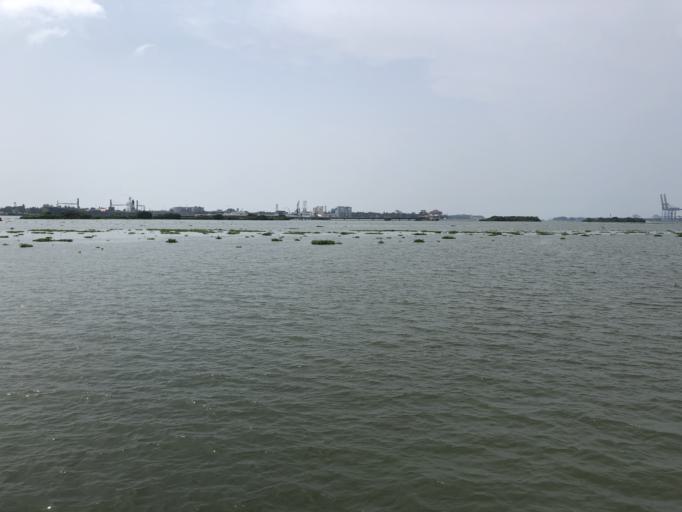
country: IN
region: Kerala
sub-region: Ernakulam
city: Cochin
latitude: 9.9754
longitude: 76.2765
